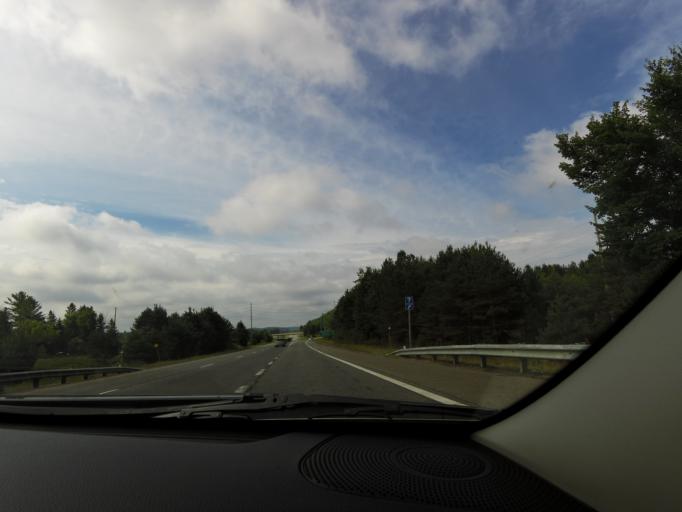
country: CA
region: Ontario
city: Huntsville
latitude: 45.3371
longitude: -79.2353
